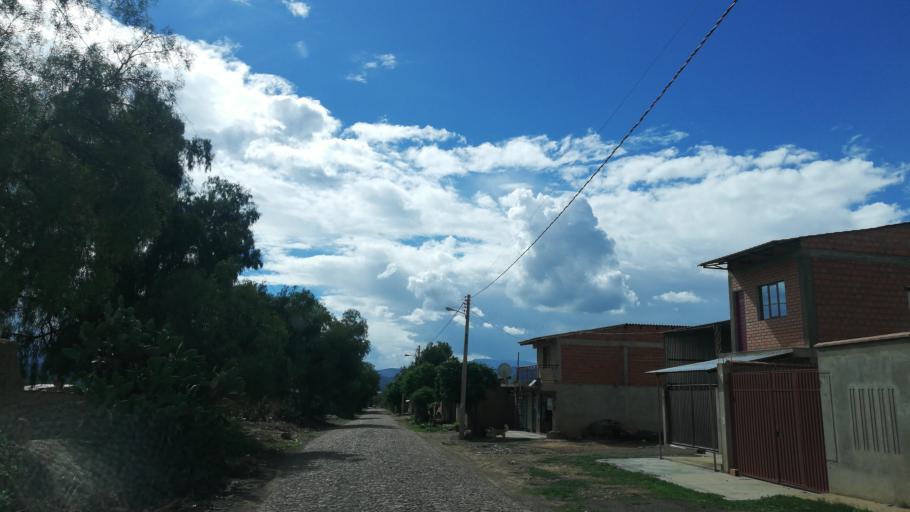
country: BO
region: Cochabamba
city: Capinota
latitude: -17.5501
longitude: -66.2238
